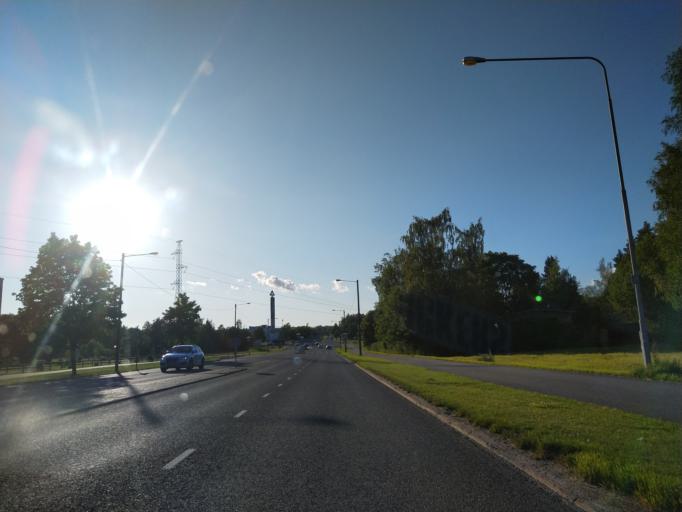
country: FI
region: Varsinais-Suomi
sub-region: Turku
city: Kaarina
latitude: 60.4441
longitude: 22.3320
